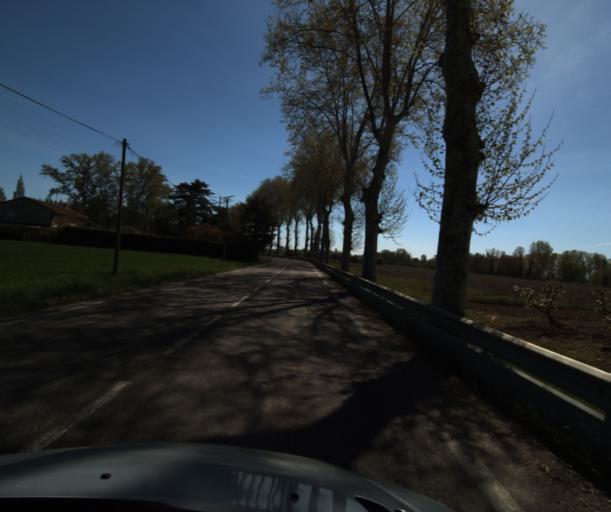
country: FR
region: Midi-Pyrenees
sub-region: Departement du Tarn-et-Garonne
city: Lafrancaise
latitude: 44.0847
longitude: 1.2745
